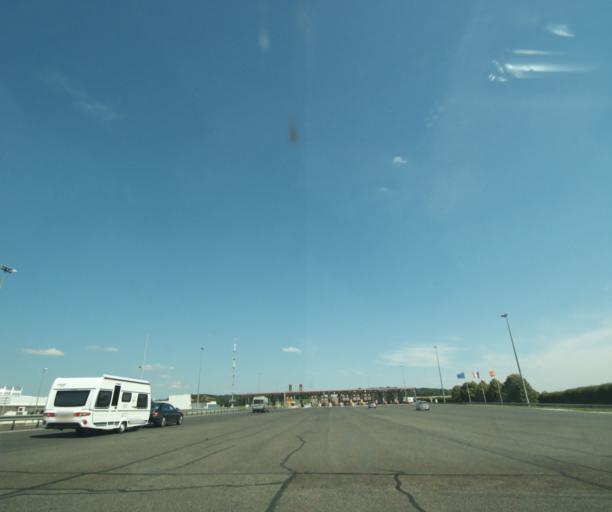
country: FR
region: Lorraine
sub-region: Departement de Meurthe-et-Moselle
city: Dommartin-les-Toul
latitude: 48.6283
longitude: 5.8842
